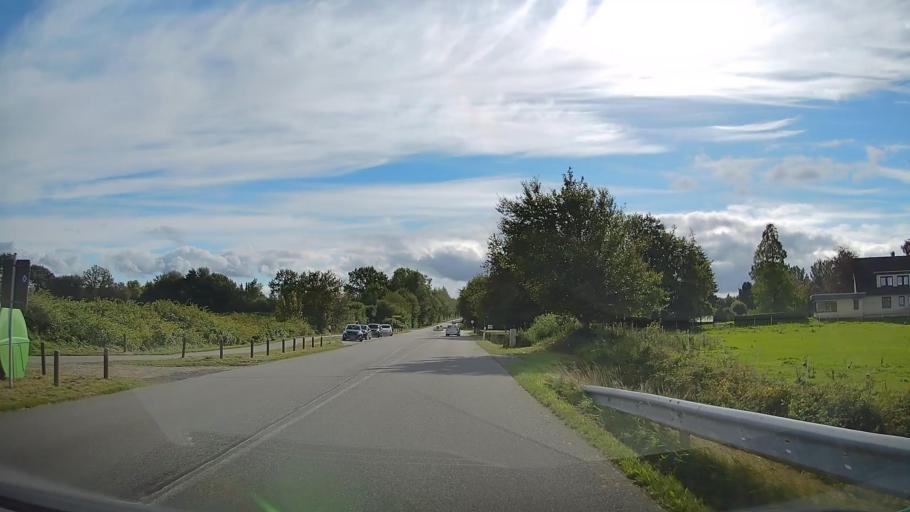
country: DE
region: Schleswig-Holstein
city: Glucksburg
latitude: 54.8522
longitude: 9.5868
